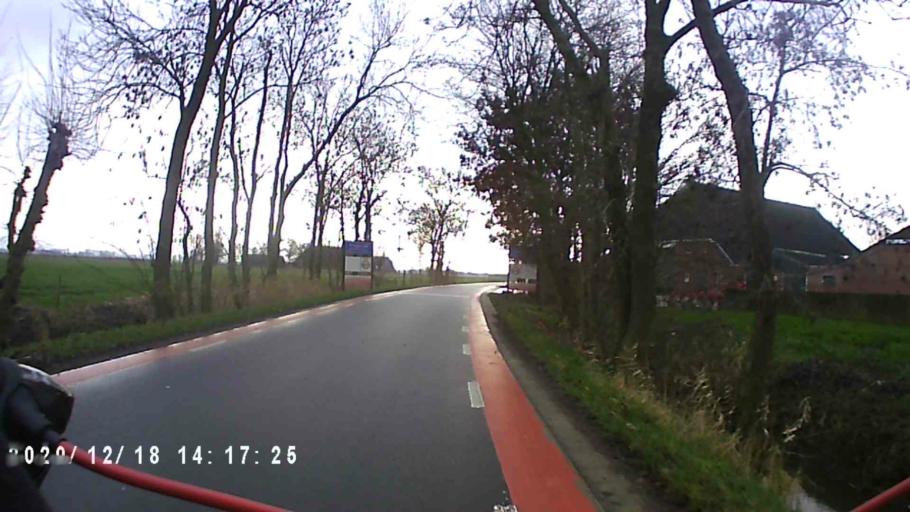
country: NL
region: Groningen
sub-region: Gemeente Bedum
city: Bedum
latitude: 53.2621
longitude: 6.6449
